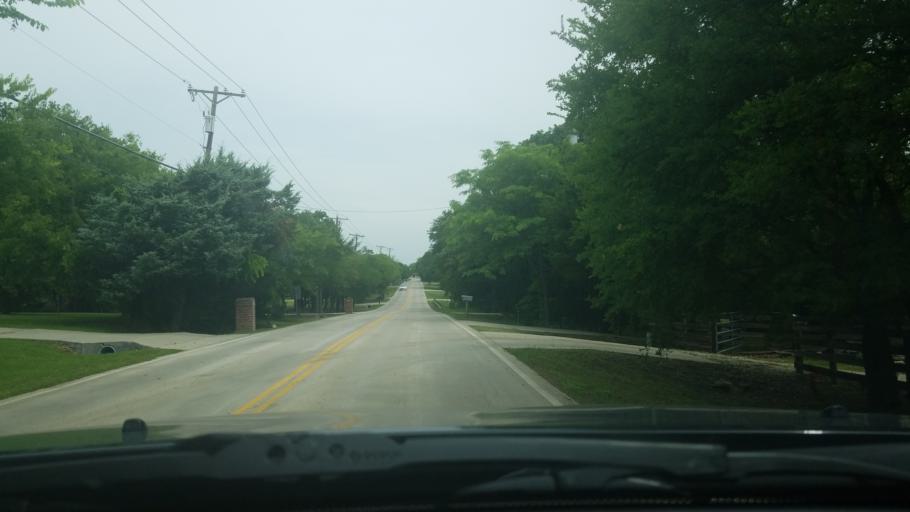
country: US
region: Texas
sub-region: Denton County
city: Lake Dallas
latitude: 33.1125
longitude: -97.0190
